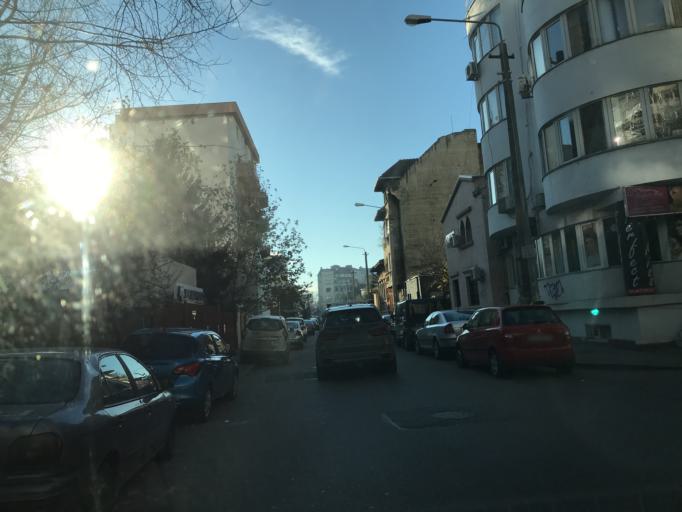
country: RO
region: Bucuresti
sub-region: Municipiul Bucuresti
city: Bucuresti
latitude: 44.4519
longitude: 26.0781
